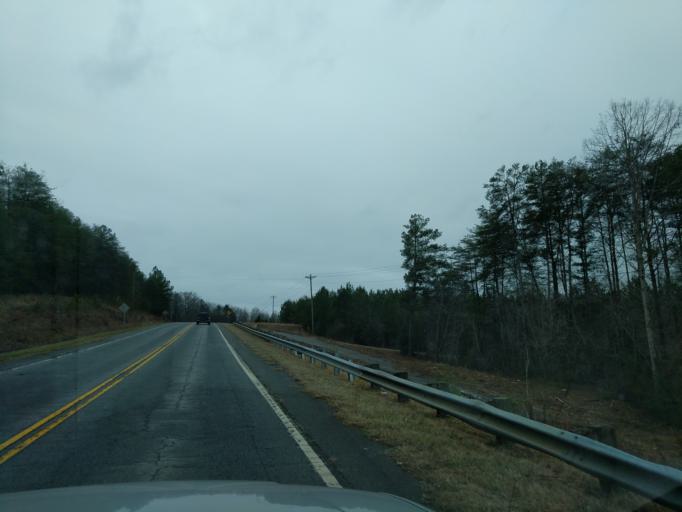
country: US
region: South Carolina
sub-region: Oconee County
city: Walhalla
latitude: 34.8406
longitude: -83.0376
